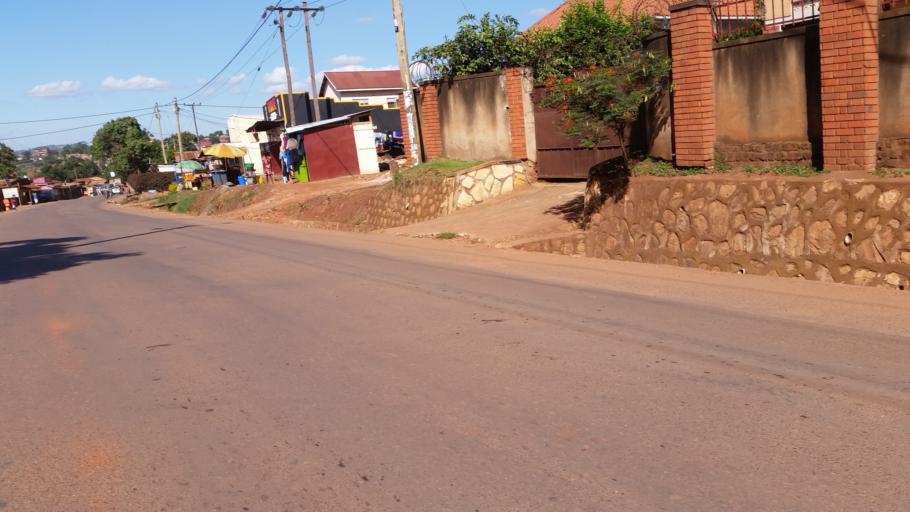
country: UG
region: Central Region
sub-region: Wakiso District
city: Kireka
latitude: 0.3445
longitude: 32.6491
